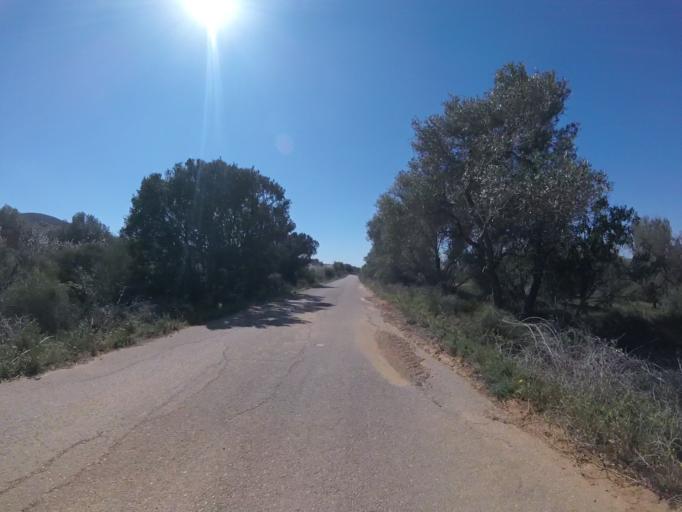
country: ES
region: Valencia
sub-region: Provincia de Castello
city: Cuevas de Vinroma
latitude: 40.3848
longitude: 0.1574
